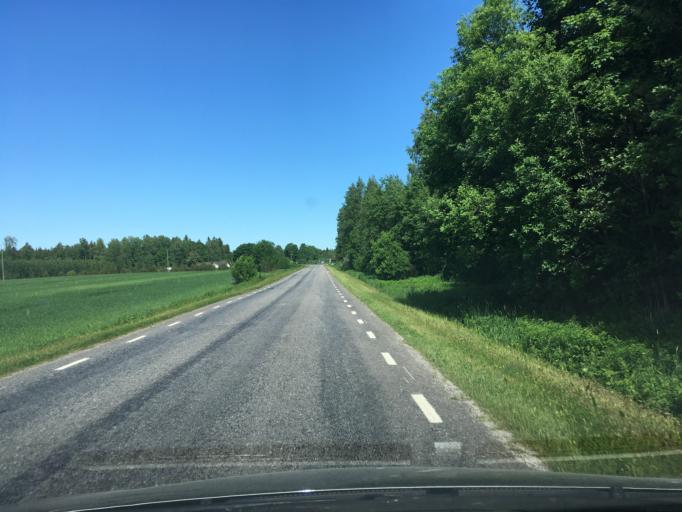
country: EE
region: Raplamaa
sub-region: Rapla vald
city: Rapla
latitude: 59.0649
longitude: 24.9129
